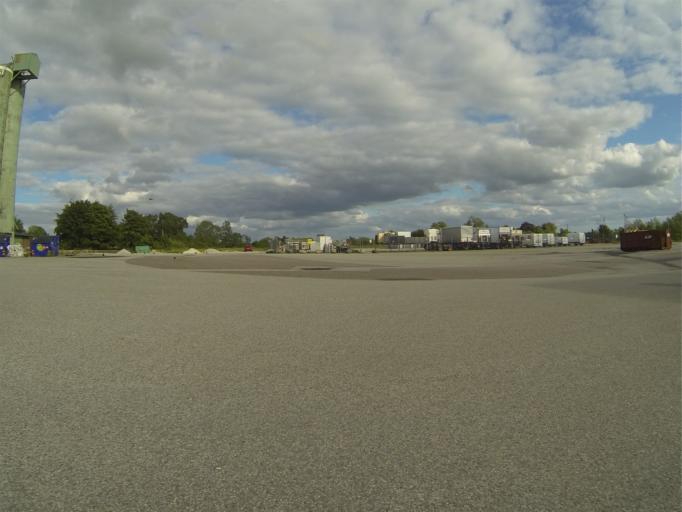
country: SE
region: Skane
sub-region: Lunds Kommun
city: Genarp
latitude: 55.6601
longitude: 13.3447
